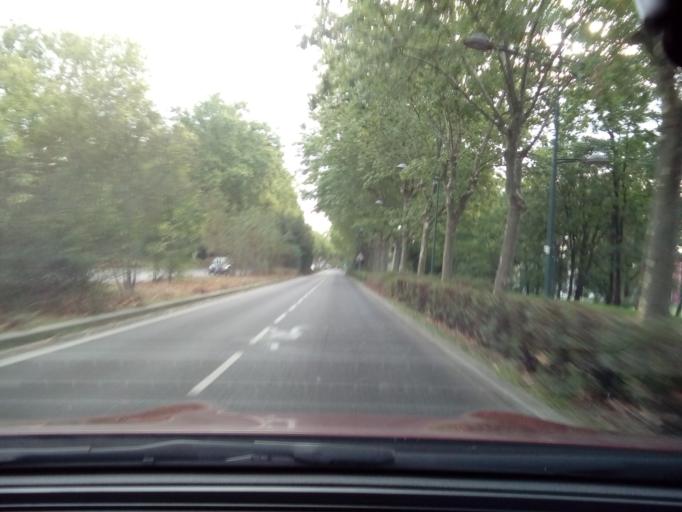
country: FR
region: Rhone-Alpes
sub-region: Departement du Rhone
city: Villeurbanne
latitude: 45.7866
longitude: 4.8765
